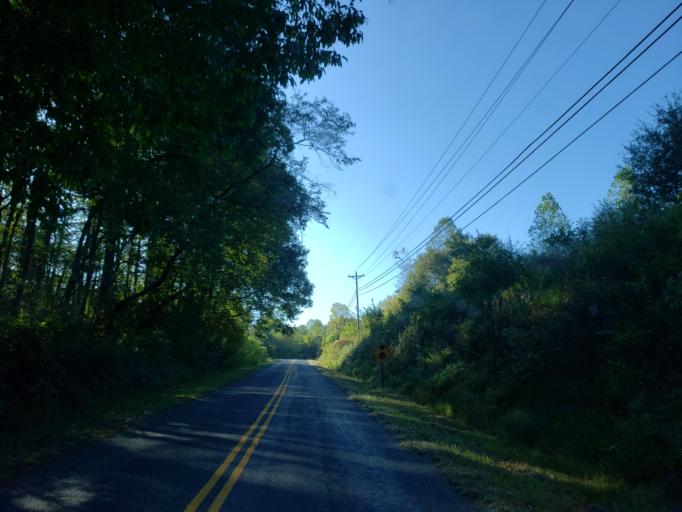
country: US
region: Georgia
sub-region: Pickens County
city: Nelson
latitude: 34.3885
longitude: -84.4094
